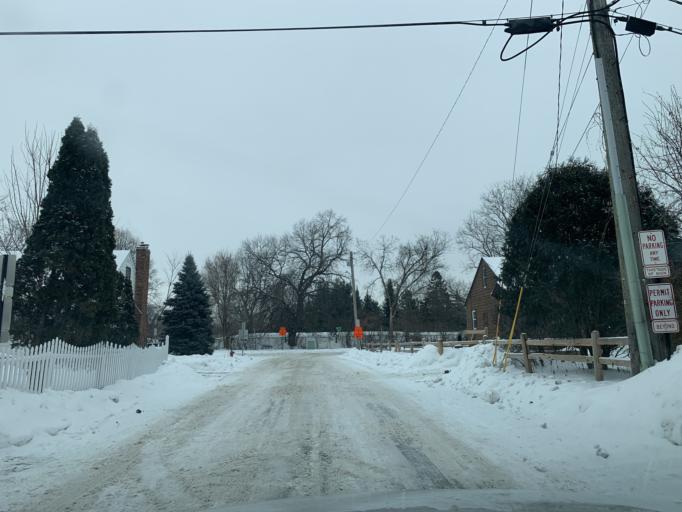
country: US
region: Minnesota
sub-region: Hennepin County
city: Saint Louis Park
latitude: 44.9414
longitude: -93.3298
